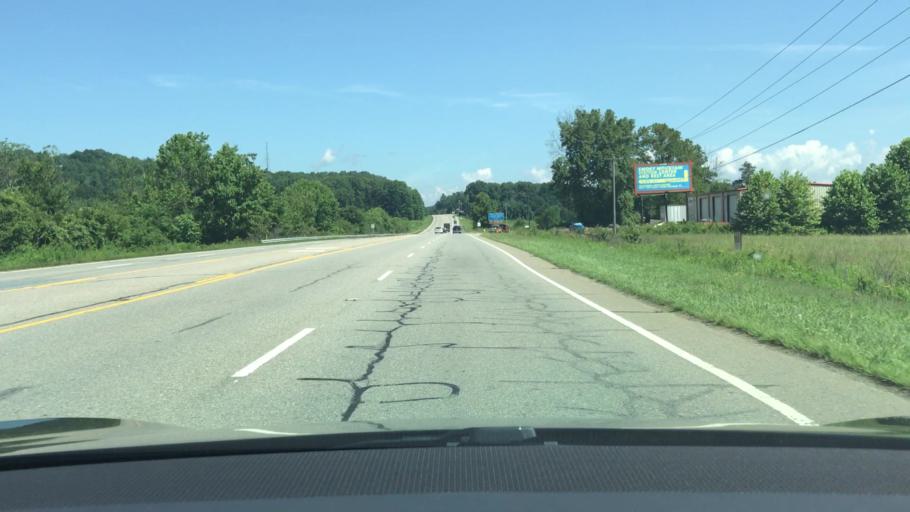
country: US
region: North Carolina
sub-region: Macon County
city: Franklin
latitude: 35.0965
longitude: -83.3842
